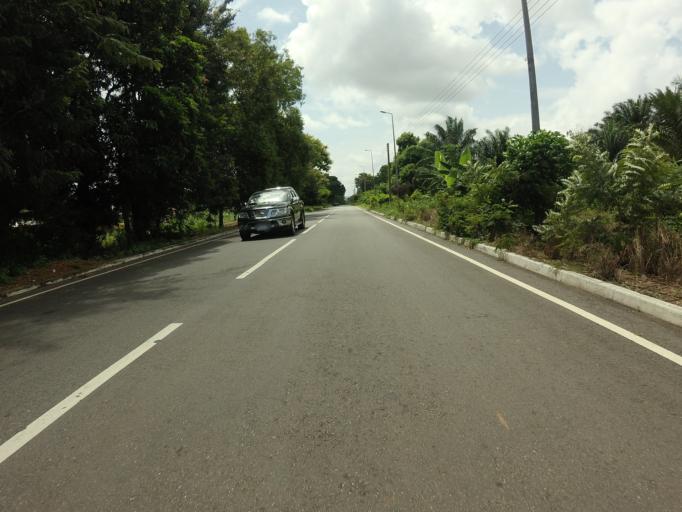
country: GH
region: Volta
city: Ho
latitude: 6.6058
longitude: 0.4593
